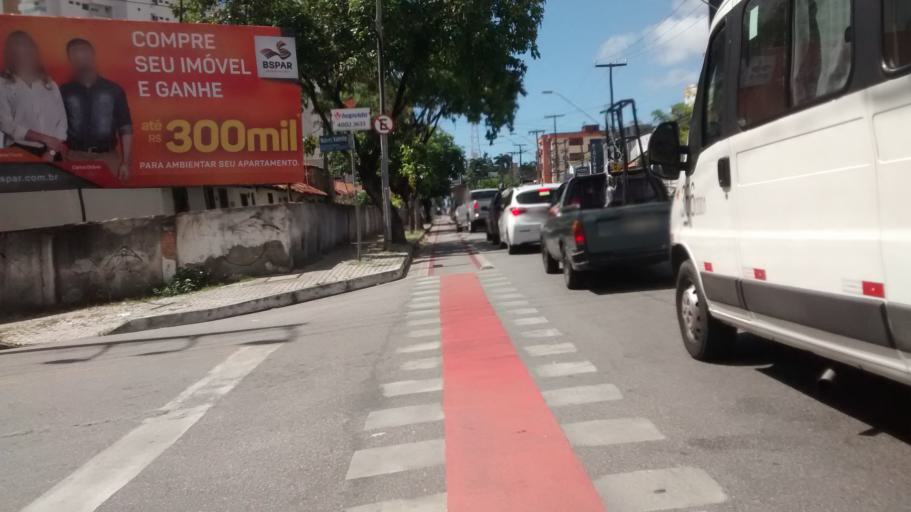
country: BR
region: Ceara
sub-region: Fortaleza
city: Fortaleza
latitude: -3.7441
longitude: -38.5064
